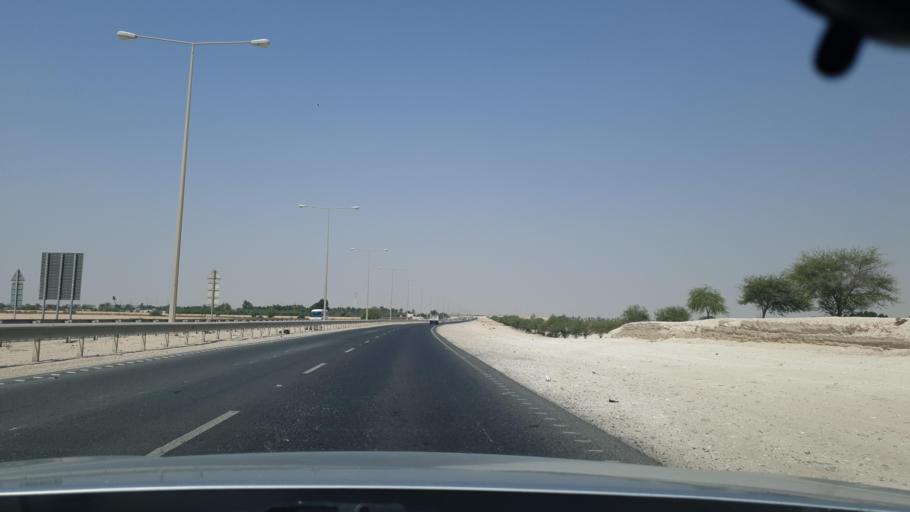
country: QA
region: Al Khawr
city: Al Khawr
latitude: 25.7237
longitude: 51.4980
